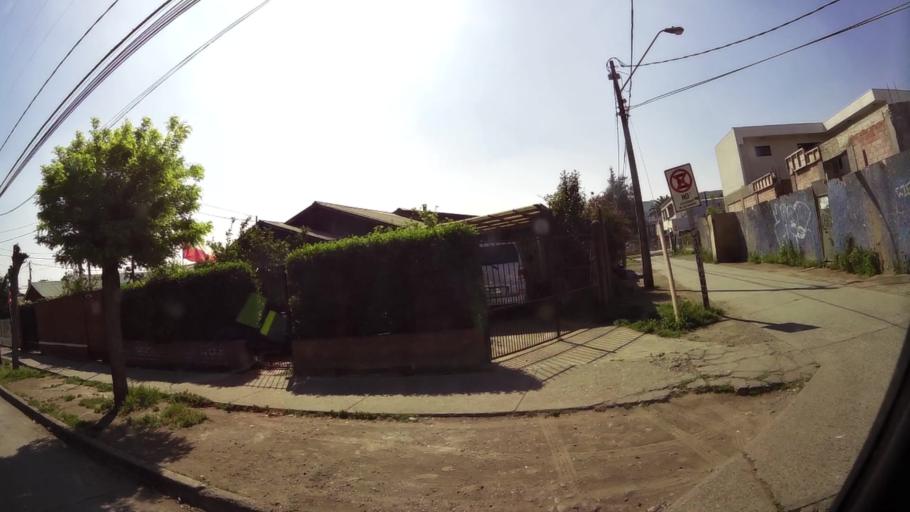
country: CL
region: Santiago Metropolitan
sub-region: Provincia de Santiago
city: Lo Prado
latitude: -33.5101
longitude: -70.7742
